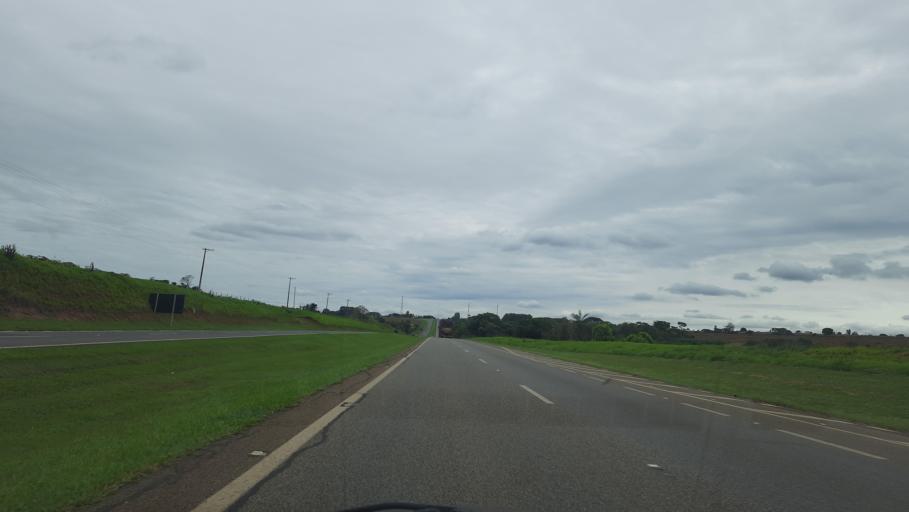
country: BR
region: Sao Paulo
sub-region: Aguai
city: Aguai
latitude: -22.2031
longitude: -46.9835
